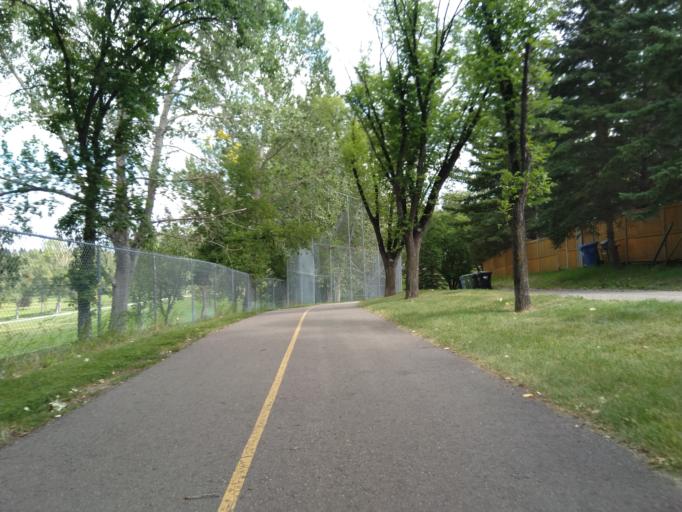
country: CA
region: Alberta
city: Calgary
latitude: 51.0771
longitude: -114.1023
